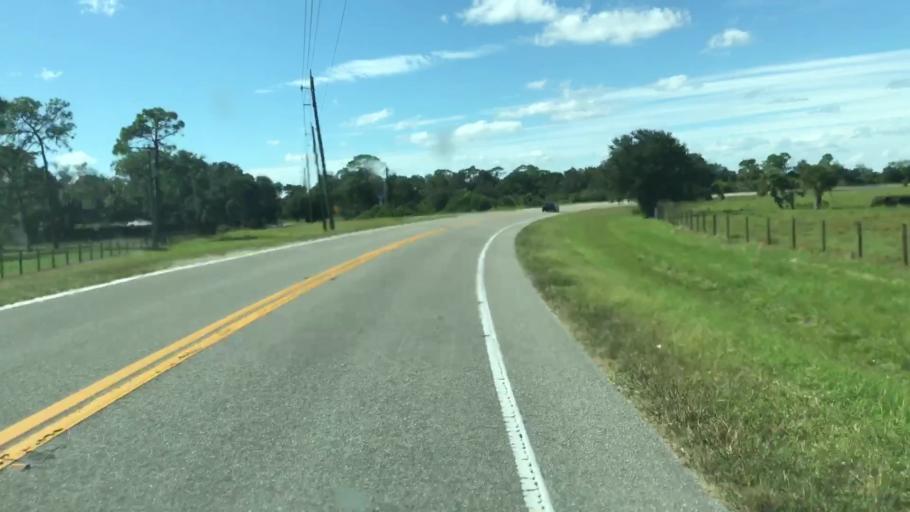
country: US
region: Florida
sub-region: Lee County
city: Olga
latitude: 26.7308
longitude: -81.7090
